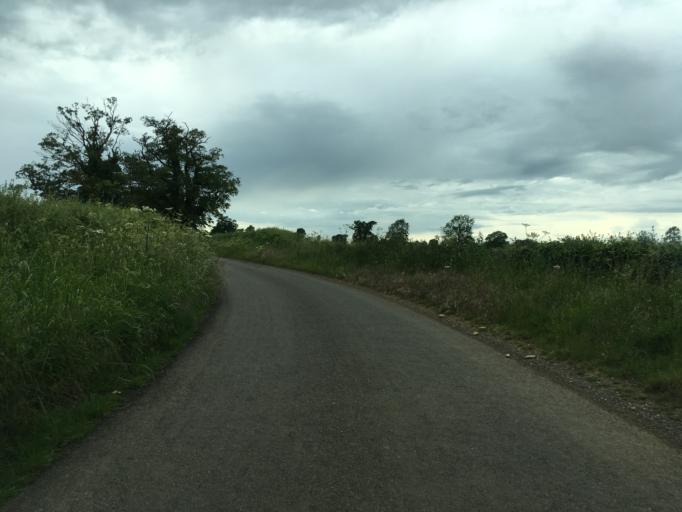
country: GB
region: England
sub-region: Wiltshire
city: Norton
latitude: 51.5916
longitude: -2.2042
